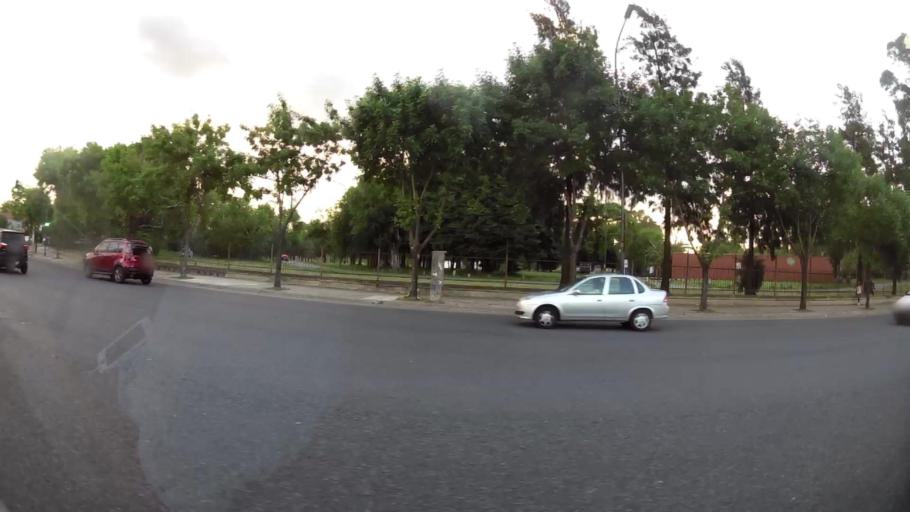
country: AR
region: Buenos Aires
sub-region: Partido de General San Martin
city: General San Martin
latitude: -34.5554
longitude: -58.4963
